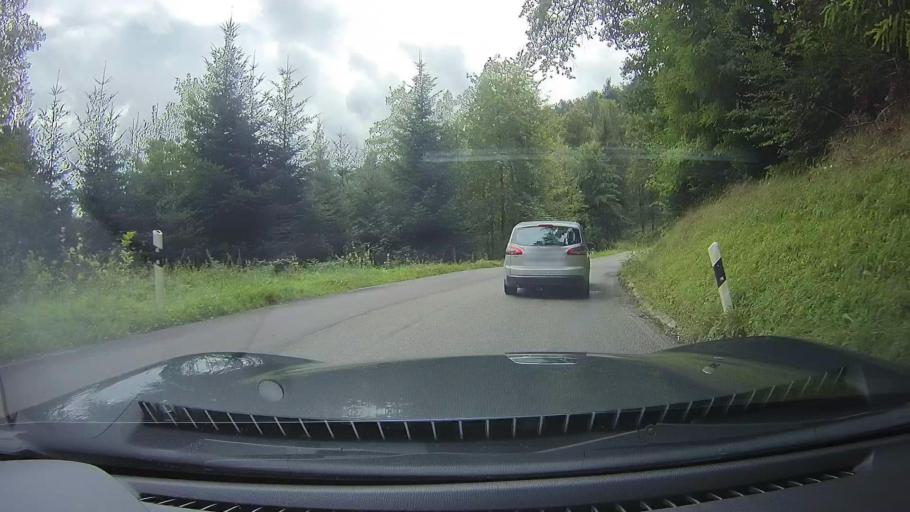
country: DE
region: Baden-Wuerttemberg
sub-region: Regierungsbezirk Stuttgart
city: Murrhardt
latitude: 48.9928
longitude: 9.5738
